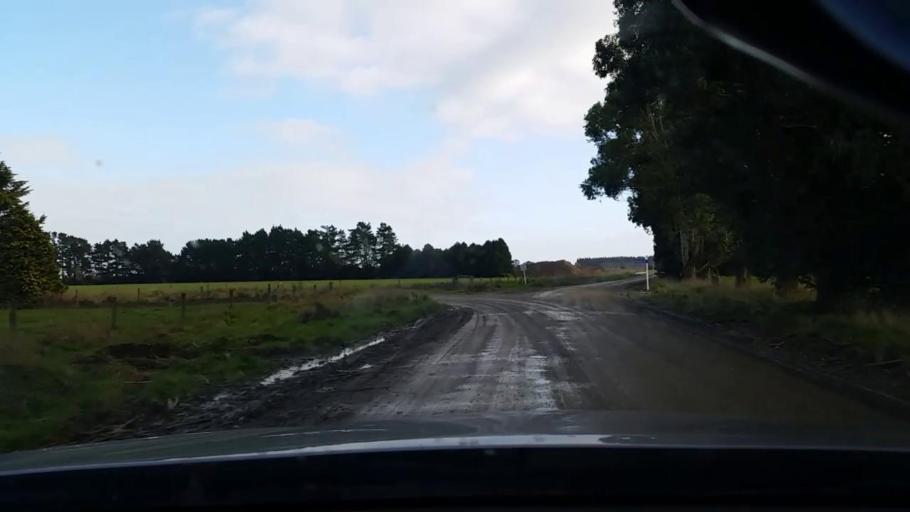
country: NZ
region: Southland
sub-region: Southland District
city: Winton
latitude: -46.2737
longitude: 168.2929
